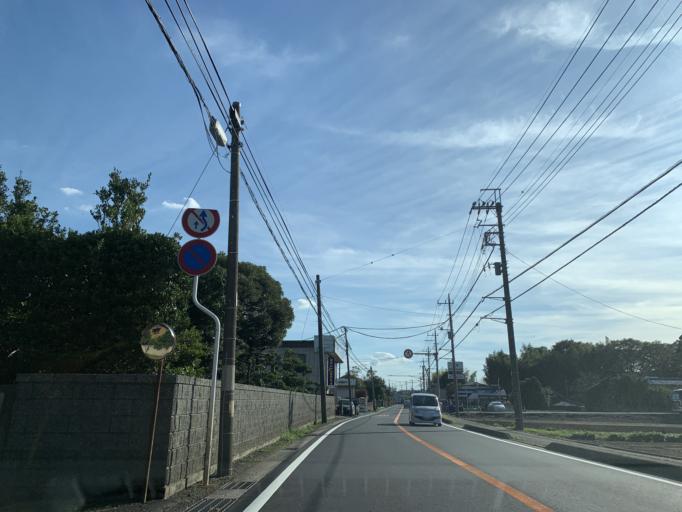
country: JP
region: Chiba
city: Nagareyama
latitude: 35.8753
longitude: 139.9041
